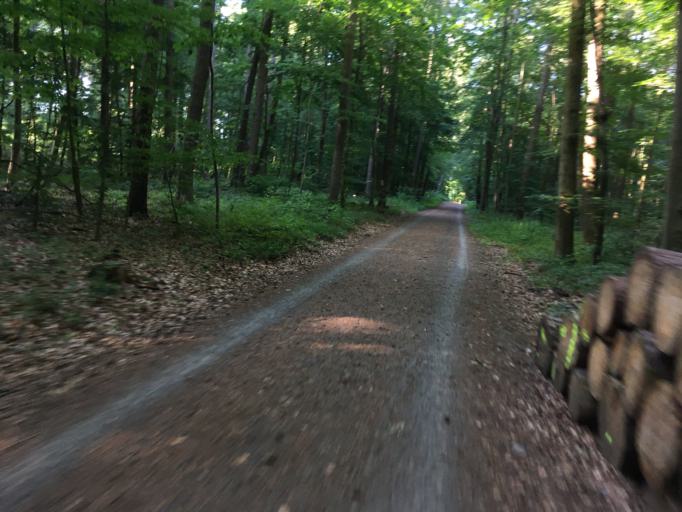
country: DE
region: Hesse
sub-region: Regierungsbezirk Darmstadt
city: Frankfurt am Main
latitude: 50.0873
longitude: 8.7178
